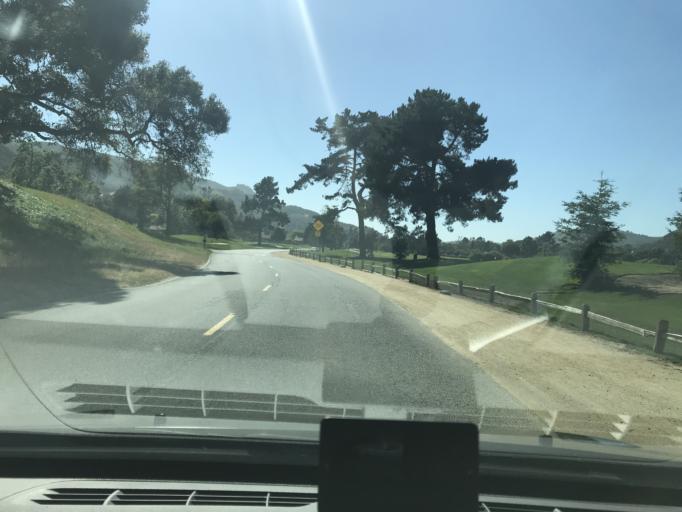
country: US
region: California
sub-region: Monterey County
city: Carmel Valley Village
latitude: 36.5179
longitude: -121.8012
